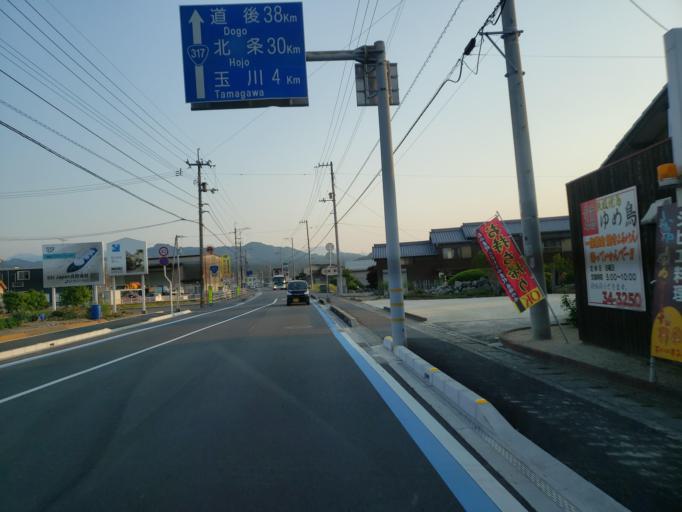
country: JP
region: Ehime
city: Hojo
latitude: 34.0403
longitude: 132.9749
